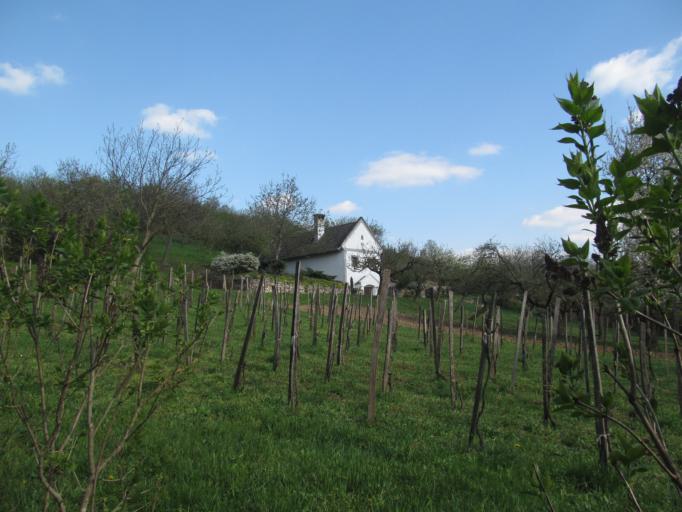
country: HU
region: Veszprem
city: Revfueloep
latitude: 46.8967
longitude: 17.5579
